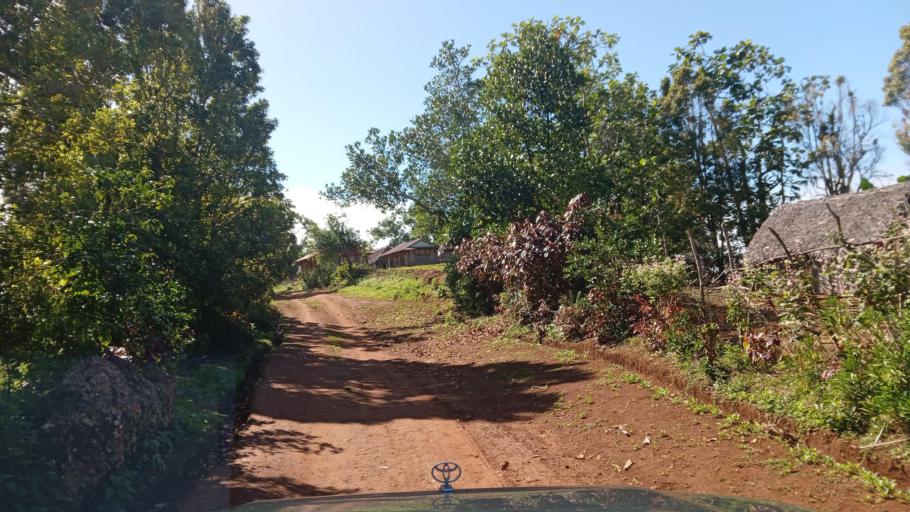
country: MG
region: Atsimo-Atsinanana
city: Vohipaho
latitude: -23.8195
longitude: 47.5485
